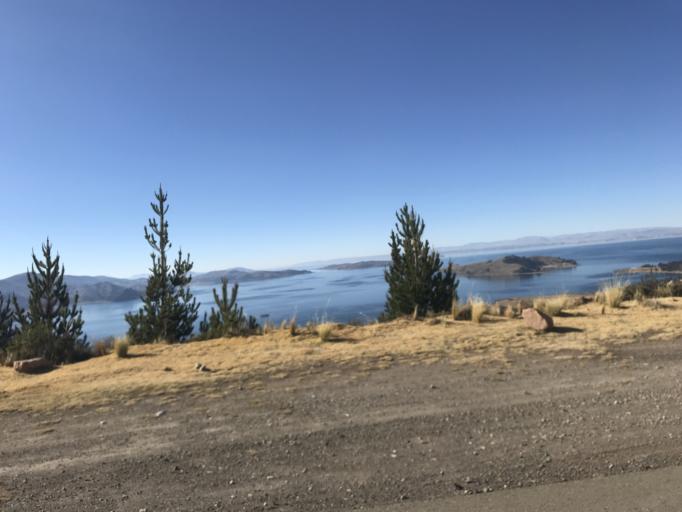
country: PE
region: Puno
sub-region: Yunguyo
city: Yunguyo
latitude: -16.1892
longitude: -68.9726
